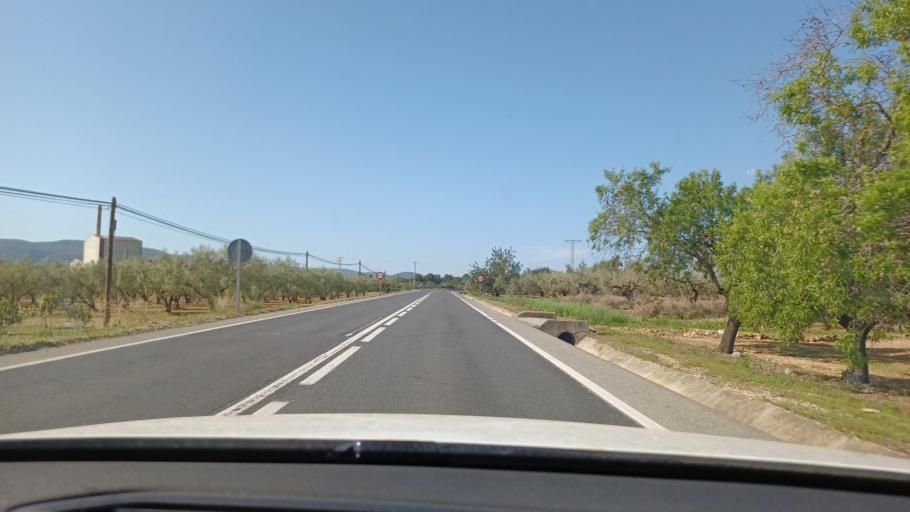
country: ES
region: Catalonia
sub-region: Provincia de Tarragona
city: Santa Barbara
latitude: 40.7037
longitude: 0.4818
